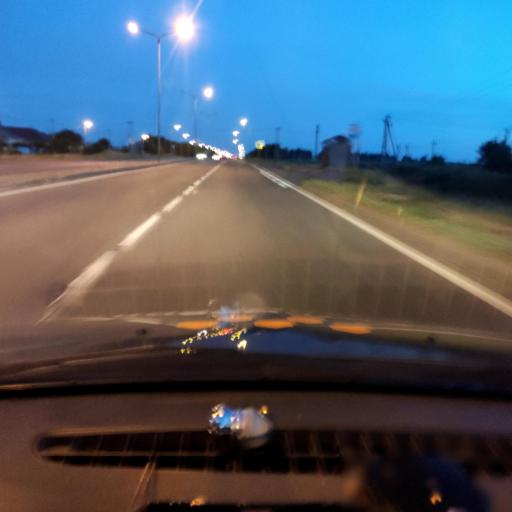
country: RU
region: Belgorod
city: Gubkin
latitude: 51.2552
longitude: 37.5272
